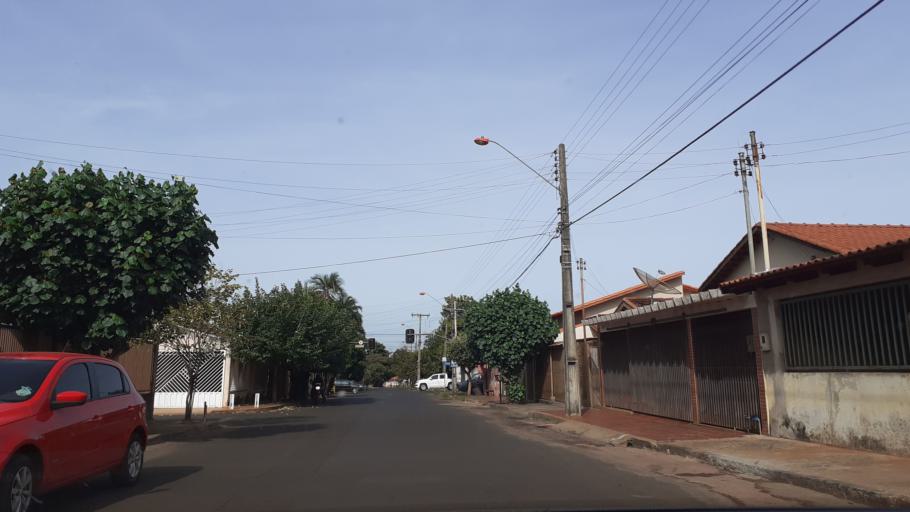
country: BR
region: Goias
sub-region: Itumbiara
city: Itumbiara
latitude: -18.4159
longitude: -49.2391
